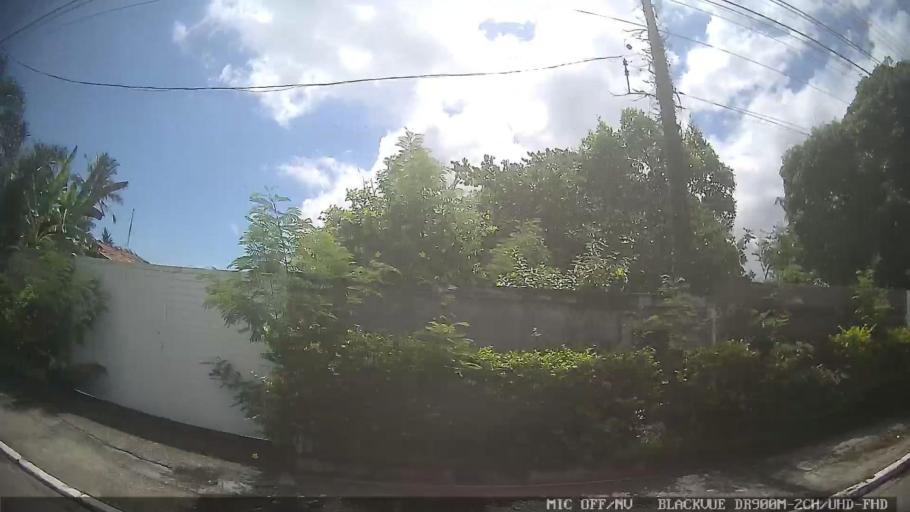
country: BR
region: Sao Paulo
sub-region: Sao Sebastiao
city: Sao Sebastiao
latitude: -23.7717
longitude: -45.4030
